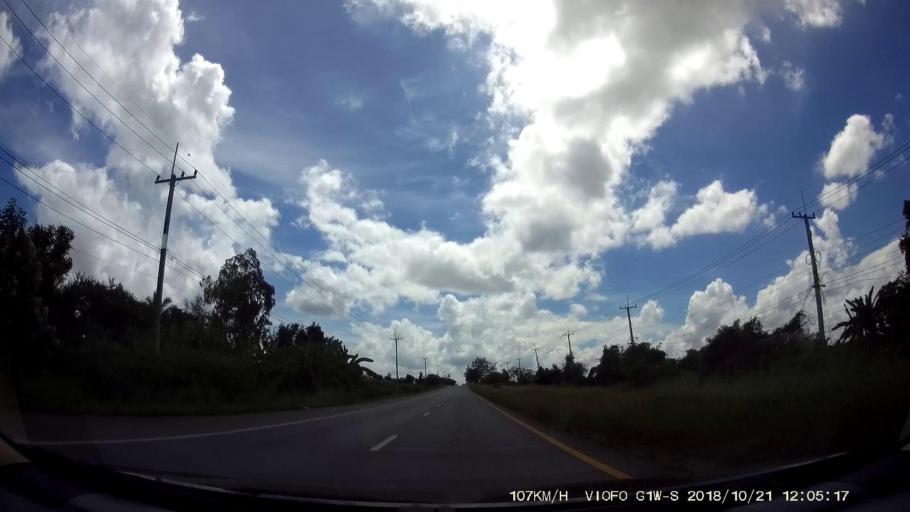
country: TH
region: Chaiyaphum
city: Chatturat
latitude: 15.4810
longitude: 101.8232
